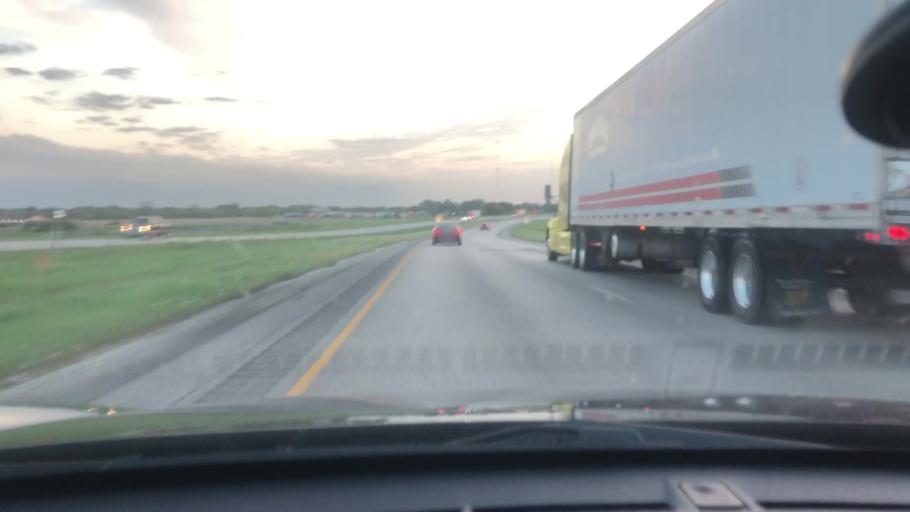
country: US
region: Texas
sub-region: Jackson County
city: Edna
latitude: 28.9681
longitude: -96.6717
